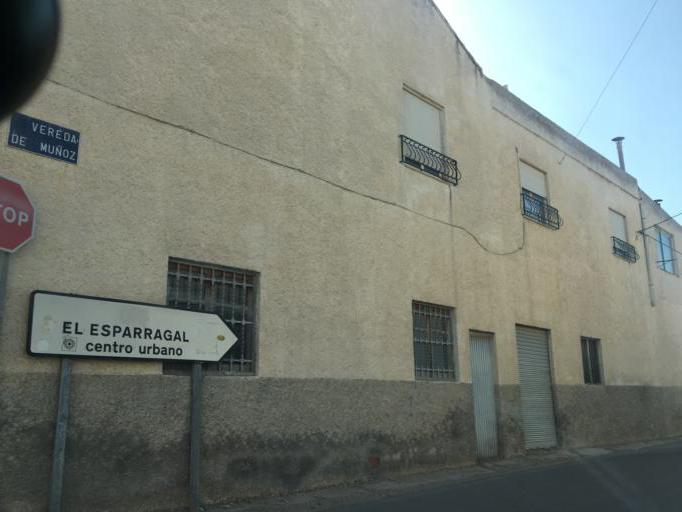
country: ES
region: Murcia
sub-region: Murcia
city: Santomera
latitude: 38.0285
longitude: -1.0656
